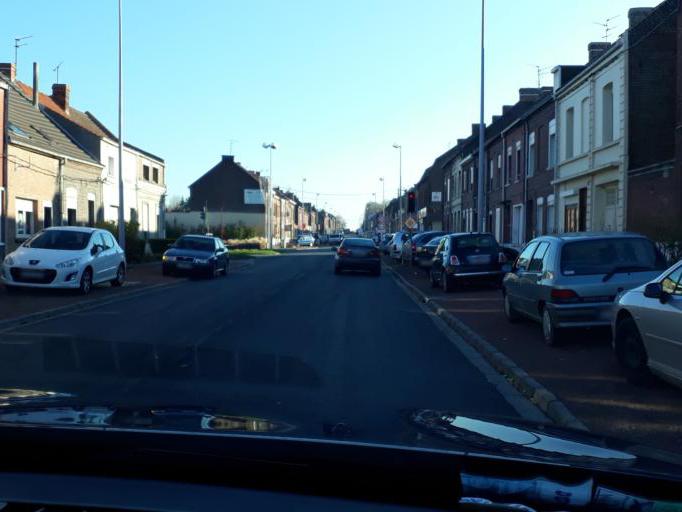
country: FR
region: Nord-Pas-de-Calais
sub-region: Departement du Nord
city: Aniche
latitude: 50.3246
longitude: 3.2517
